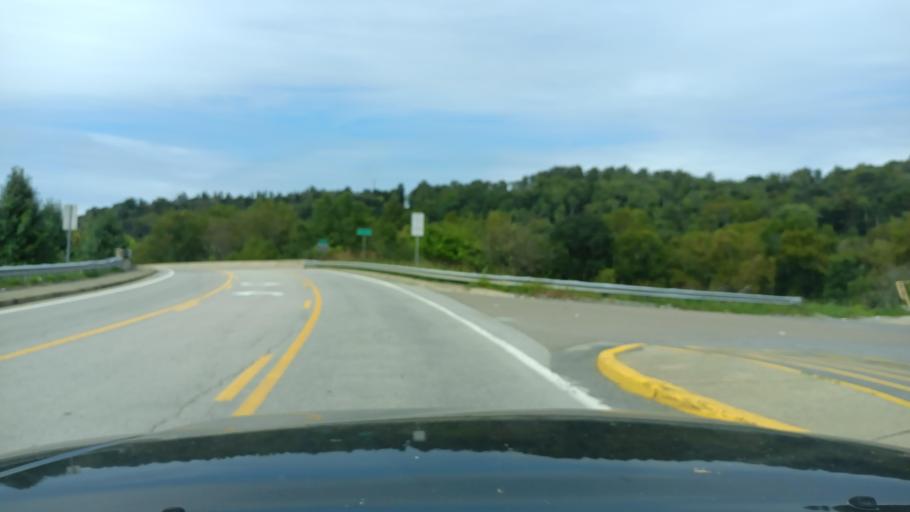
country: US
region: West Virginia
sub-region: Taylor County
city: Grafton
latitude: 39.3526
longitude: -80.0384
